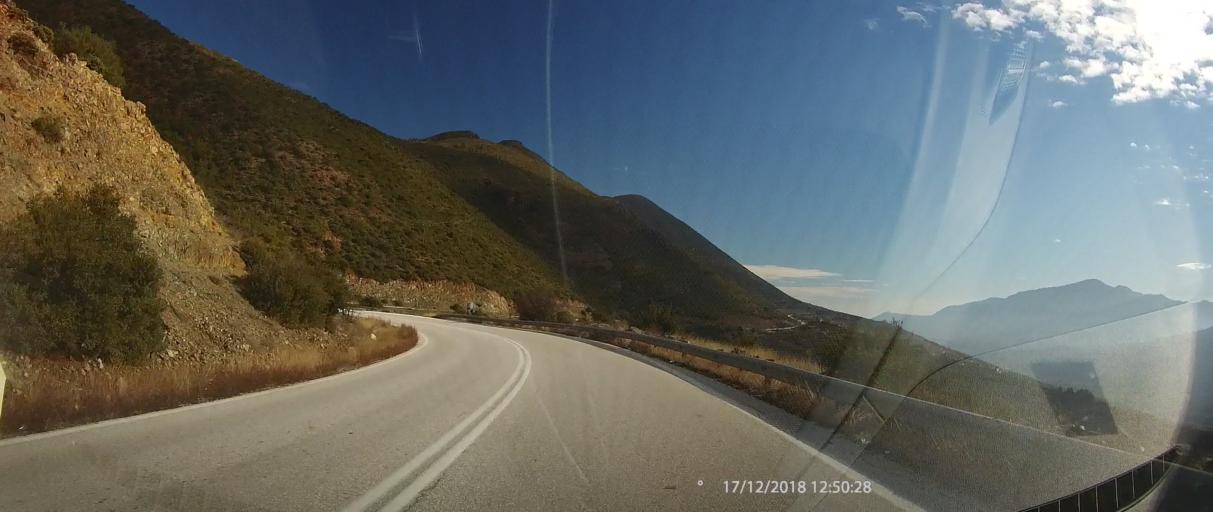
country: GR
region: Thessaly
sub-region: Trikala
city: Kastraki
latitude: 39.7718
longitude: 21.4527
